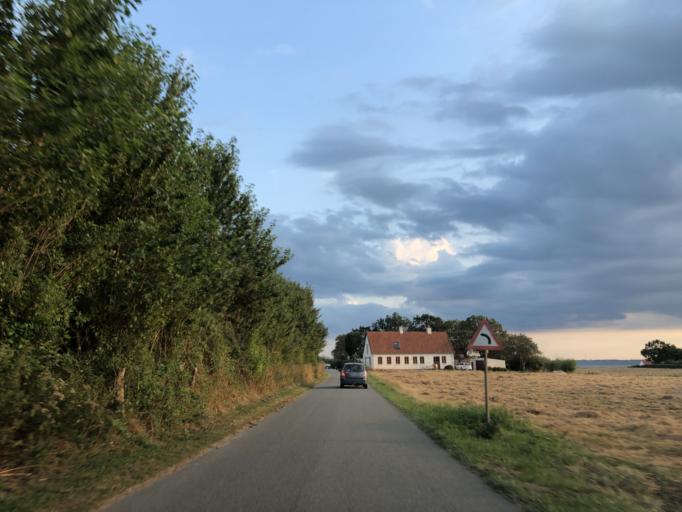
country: DK
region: South Denmark
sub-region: Kerteminde Kommune
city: Munkebo
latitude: 55.5150
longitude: 10.5957
